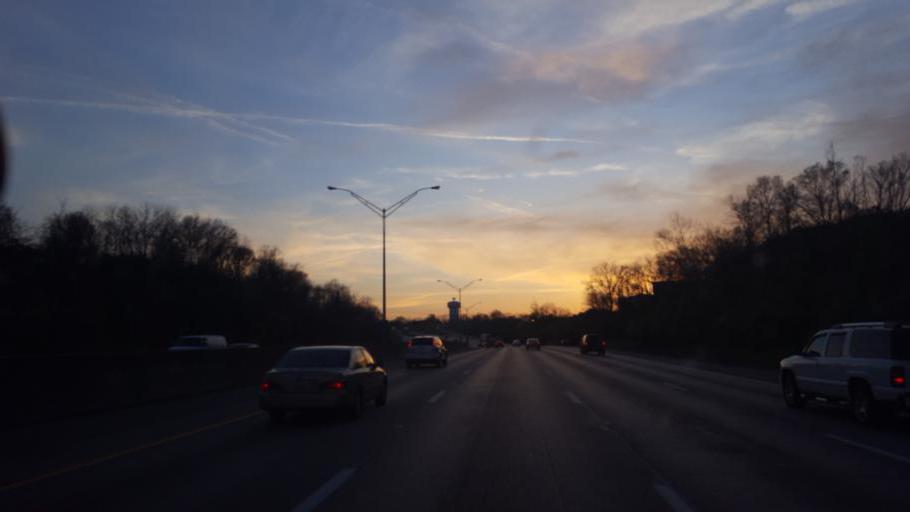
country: US
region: Kentucky
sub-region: Kenton County
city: Fort Wright
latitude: 39.0609
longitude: -84.5290
